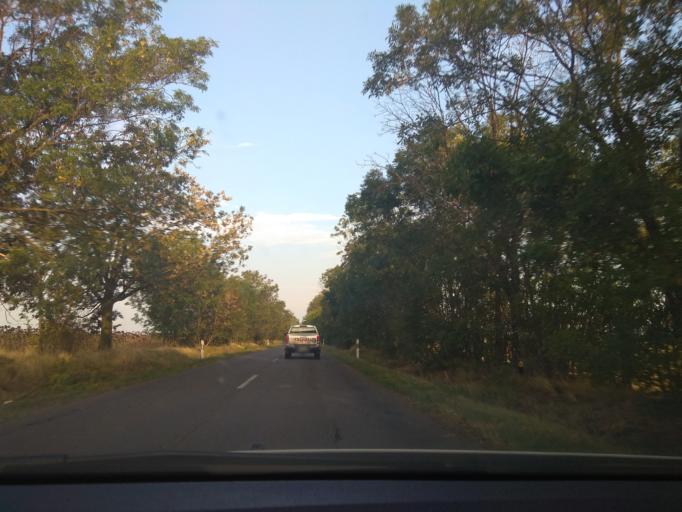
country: HU
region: Heves
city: Ostoros
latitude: 47.8287
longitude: 20.4595
